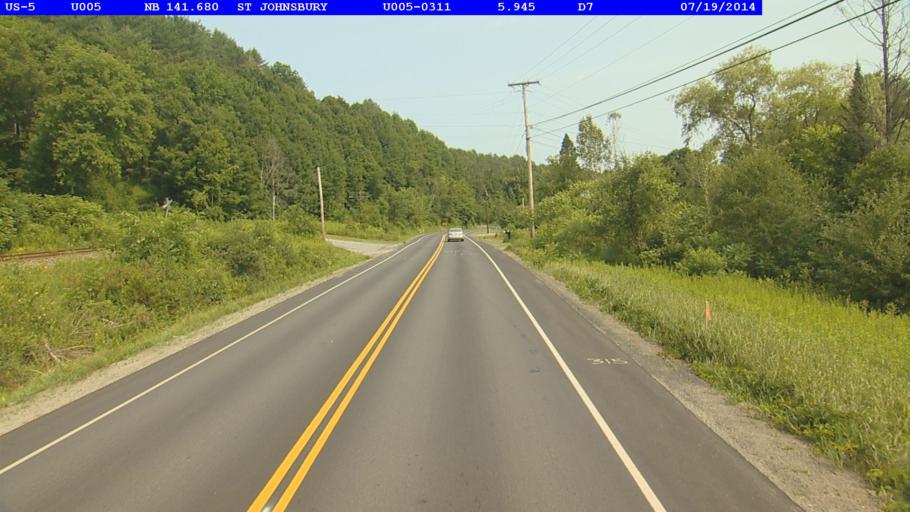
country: US
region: Vermont
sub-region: Caledonia County
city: Lyndon
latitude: 44.4762
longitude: -72.0165
